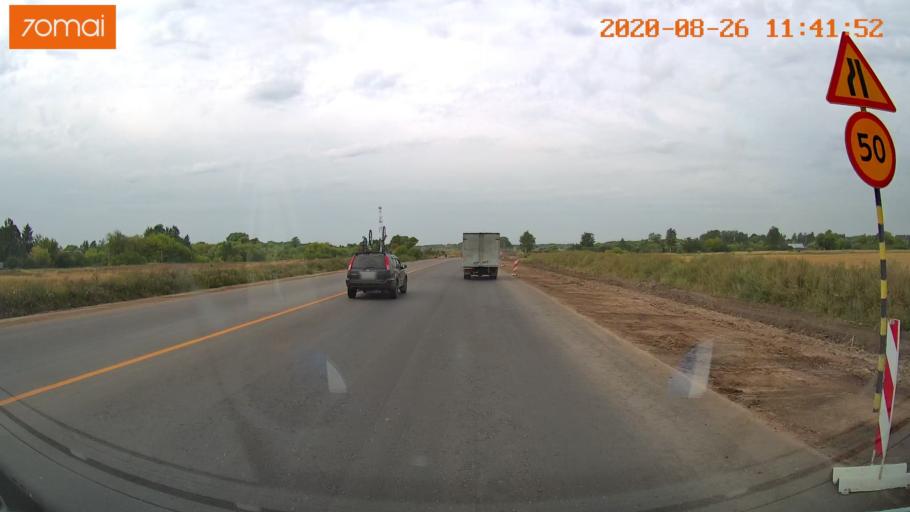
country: RU
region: Rjazan
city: Shilovo
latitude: 54.2960
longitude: 40.7028
